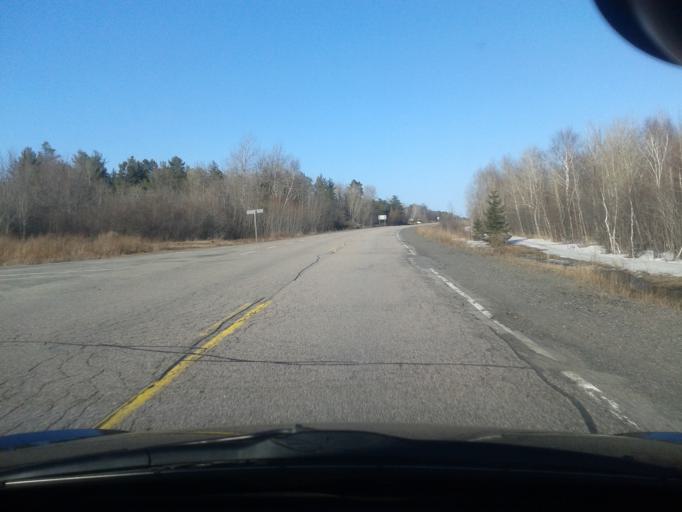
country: CA
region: Ontario
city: Greater Sudbury
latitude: 46.2686
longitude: -80.2981
